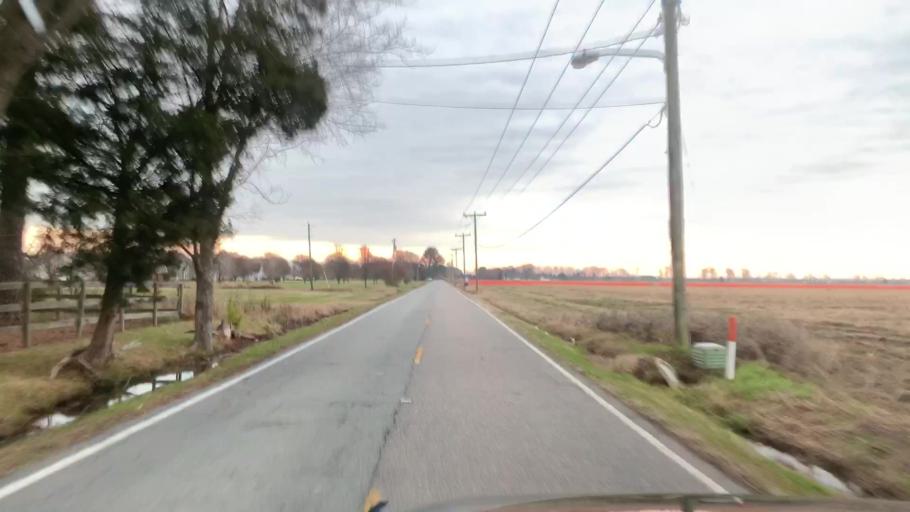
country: US
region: North Carolina
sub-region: Currituck County
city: Moyock
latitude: 36.6300
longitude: -76.1745
